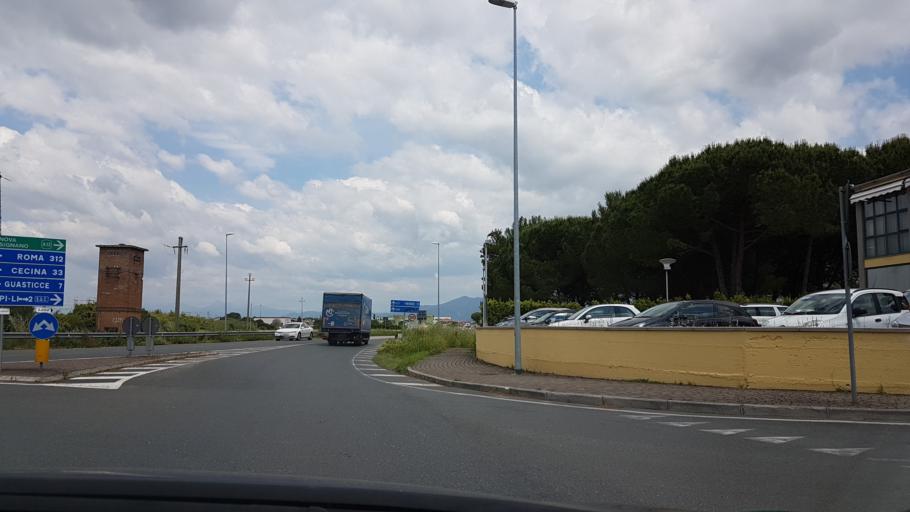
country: IT
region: Tuscany
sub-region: Provincia di Livorno
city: Collesalvetti
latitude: 43.5886
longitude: 10.4710
